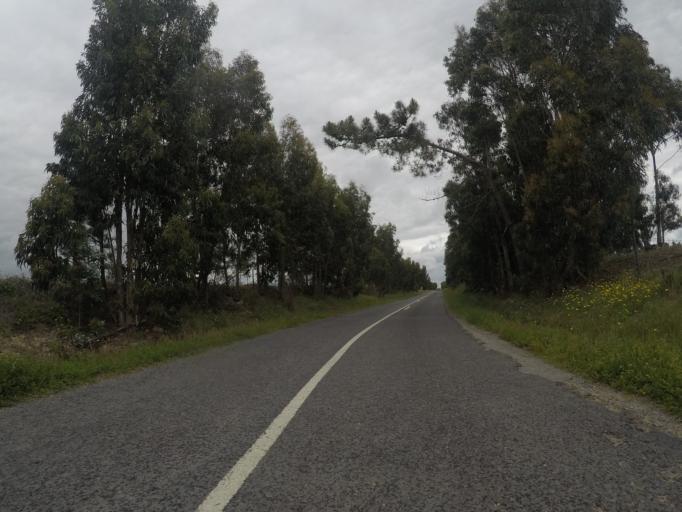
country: PT
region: Beja
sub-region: Odemira
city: Sao Teotonio
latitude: 37.5941
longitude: -8.7771
